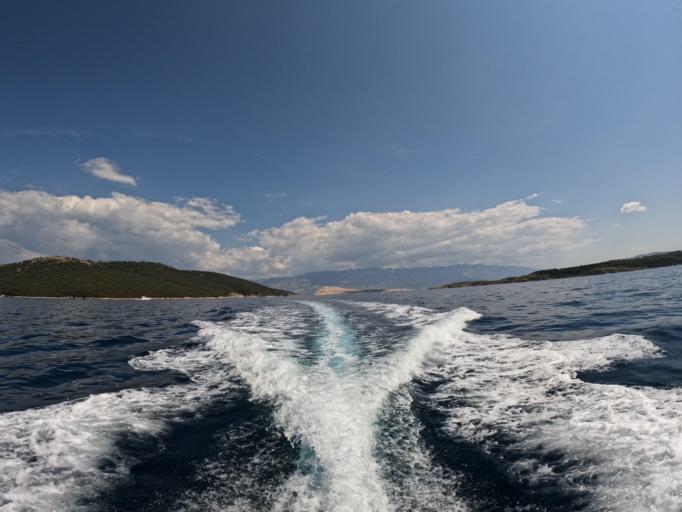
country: HR
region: Primorsko-Goranska
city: Lopar
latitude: 44.8562
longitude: 14.7373
